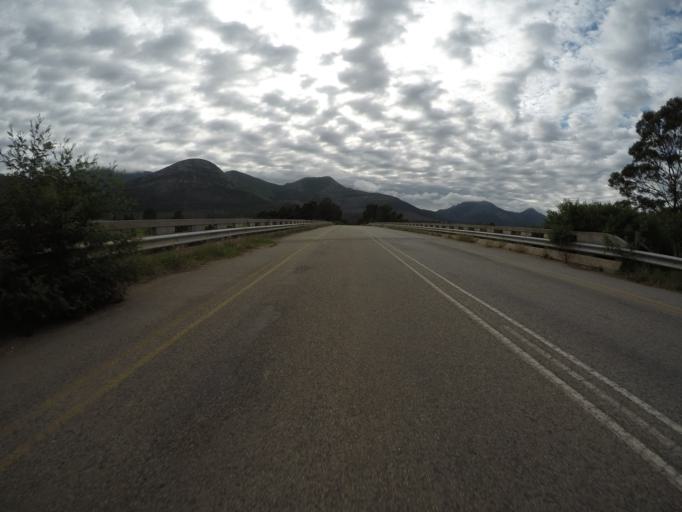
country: ZA
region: Eastern Cape
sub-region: Cacadu District Municipality
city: Kareedouw
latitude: -34.0138
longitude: 24.3067
